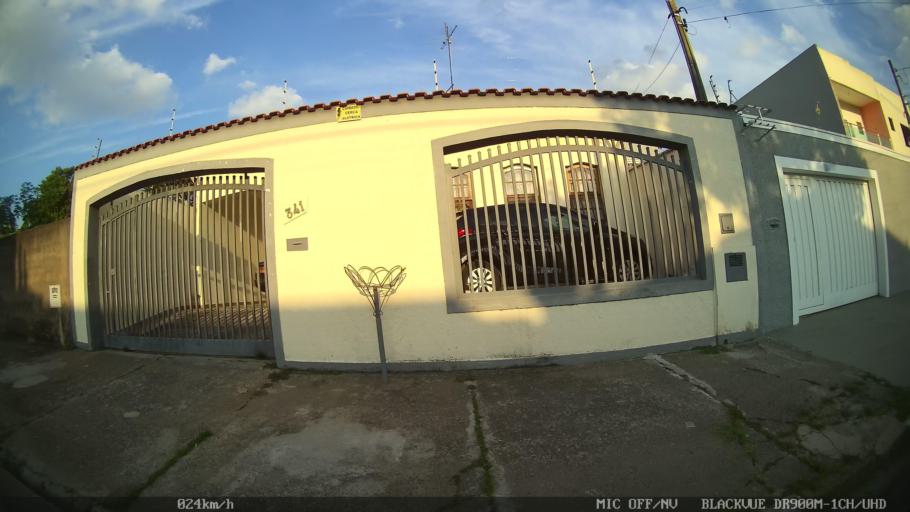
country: BR
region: Sao Paulo
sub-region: Hortolandia
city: Hortolandia
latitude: -22.8908
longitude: -47.1470
